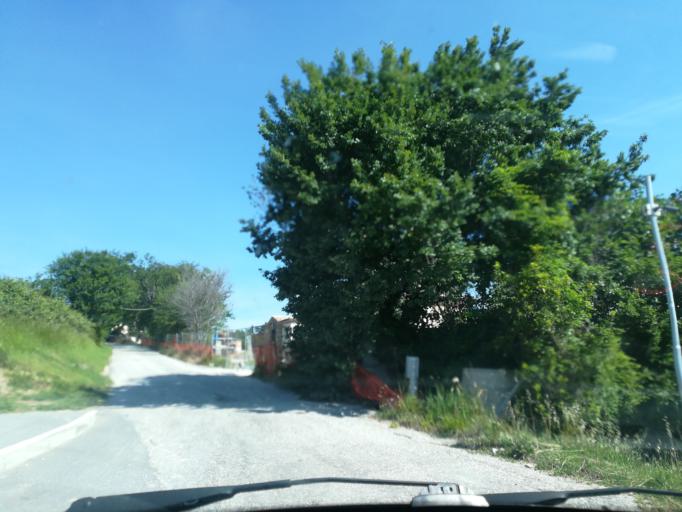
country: IT
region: The Marches
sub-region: Provincia di Macerata
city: Piediripa
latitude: 43.2895
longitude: 13.4775
